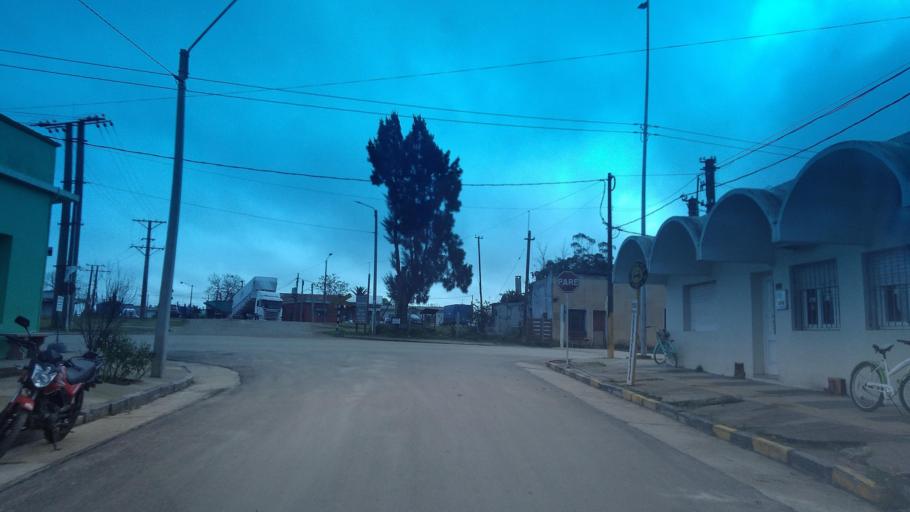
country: UY
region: Canelones
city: Tala
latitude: -34.1964
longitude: -55.7409
